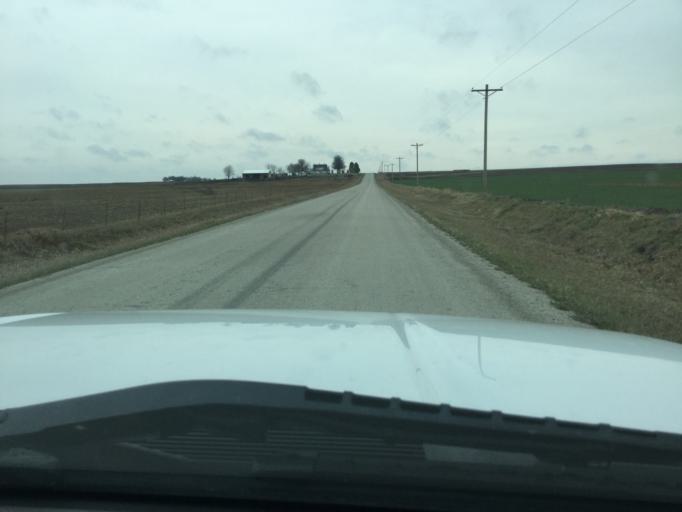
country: US
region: Kansas
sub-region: Nemaha County
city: Sabetha
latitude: 39.8594
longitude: -95.7142
